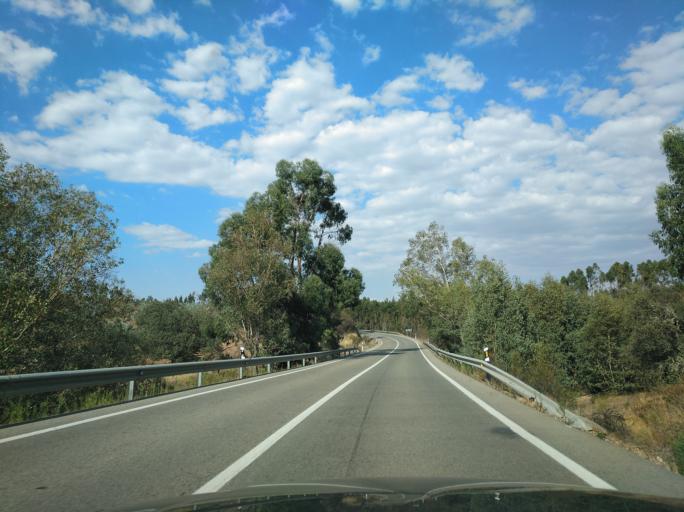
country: ES
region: Andalusia
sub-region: Provincia de Huelva
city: Santa Barbara de Casa
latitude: 37.8249
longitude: -7.2087
